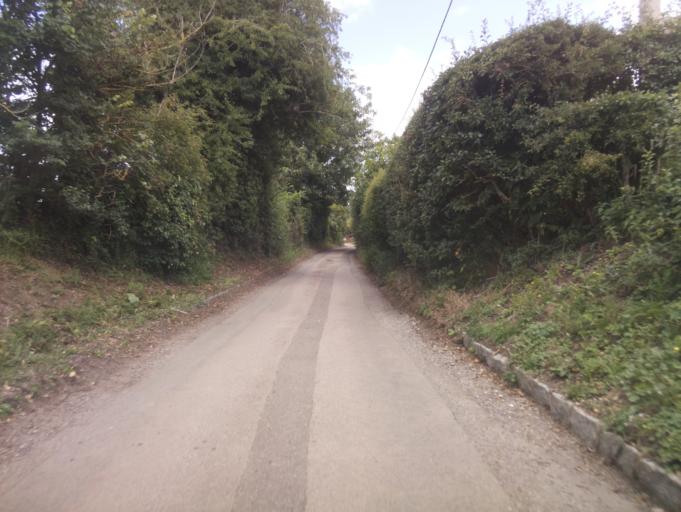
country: GB
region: England
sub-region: Buckinghamshire
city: Winslow
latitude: 51.9368
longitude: -0.8284
